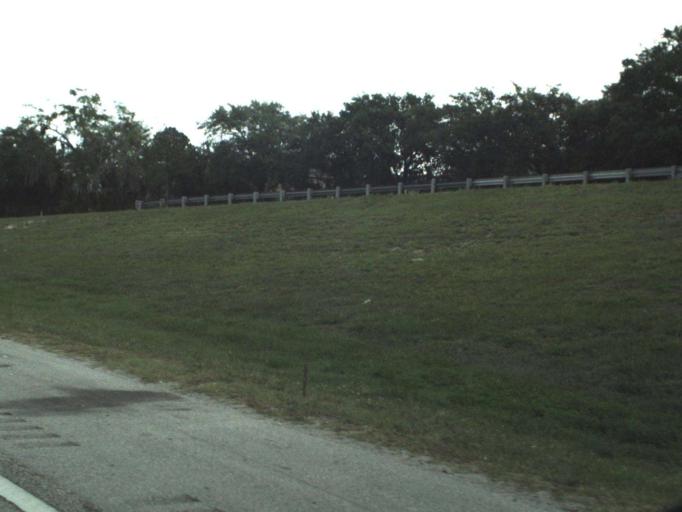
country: US
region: Florida
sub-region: Seminole County
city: Altamonte Springs
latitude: 28.6624
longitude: -81.3884
